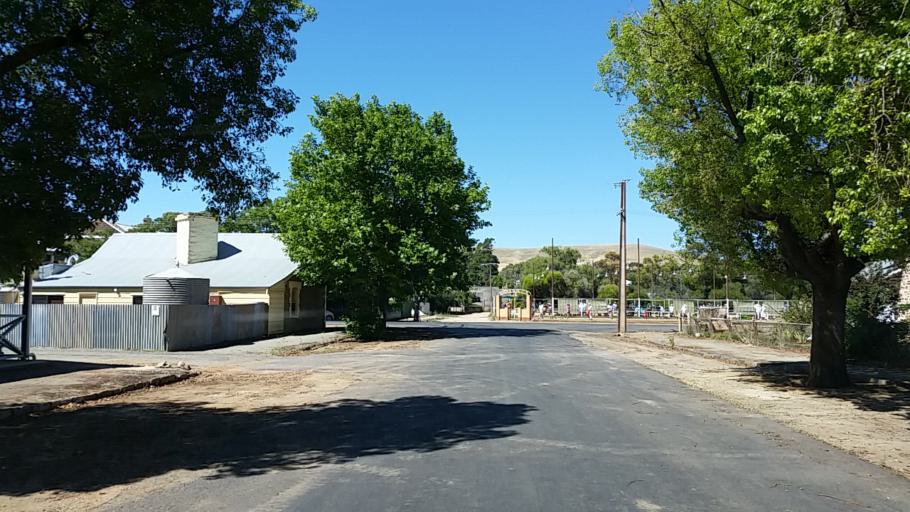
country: AU
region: South Australia
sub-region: Clare and Gilbert Valleys
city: Clare
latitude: -33.6834
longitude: 138.9397
